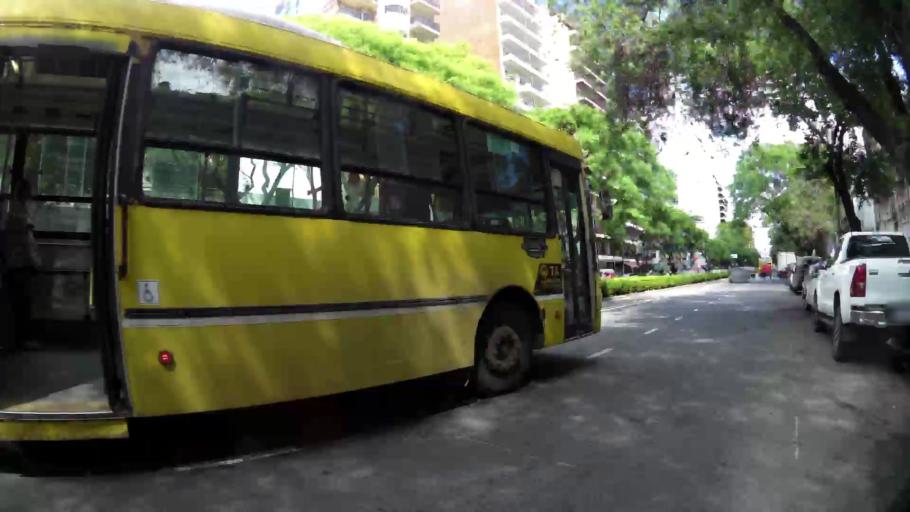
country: AR
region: Santa Fe
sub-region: Departamento de Rosario
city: Rosario
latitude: -32.9586
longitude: -60.6330
